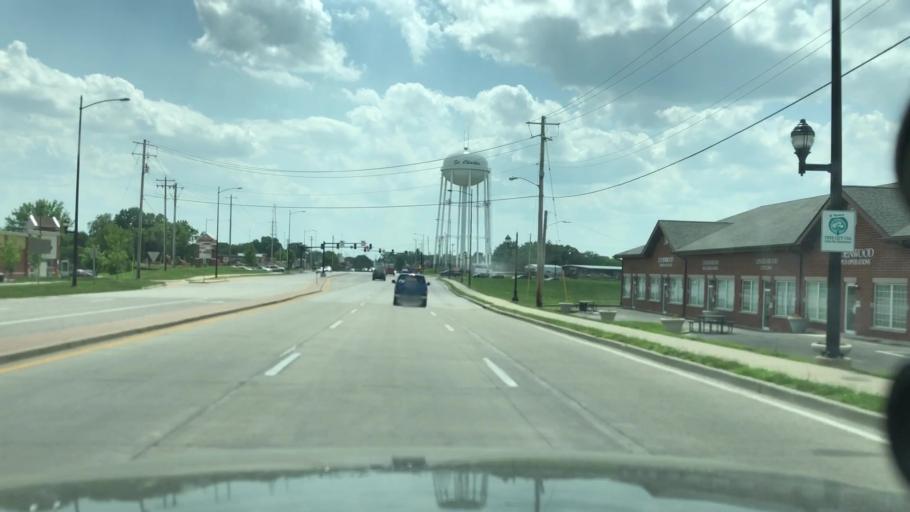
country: US
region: Missouri
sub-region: Saint Charles County
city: Saint Charles
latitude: 38.7839
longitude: -90.5032
